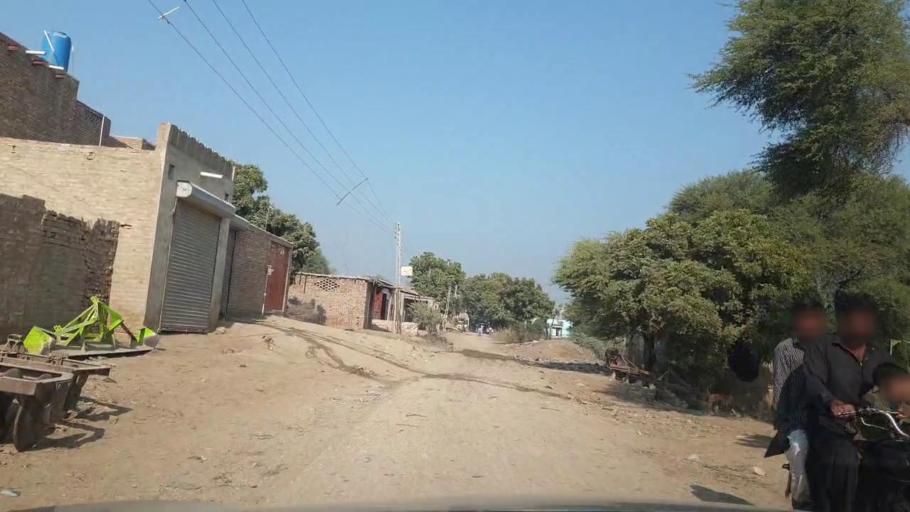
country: PK
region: Sindh
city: Tando Allahyar
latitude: 25.5022
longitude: 68.7523
